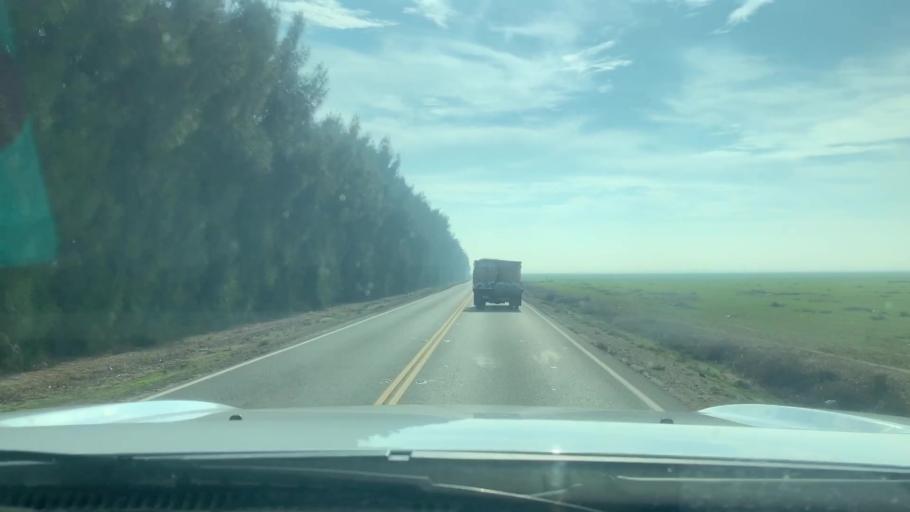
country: US
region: California
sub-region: Kern County
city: Lost Hills
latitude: 35.5150
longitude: -119.7513
